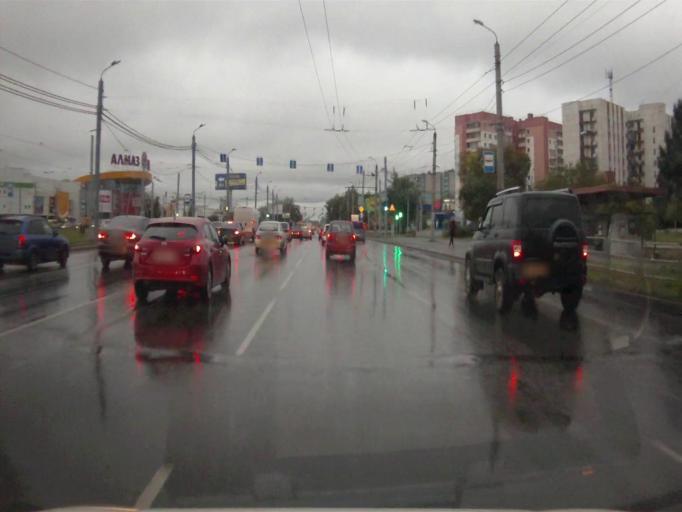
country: RU
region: Chelyabinsk
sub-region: Gorod Chelyabinsk
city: Chelyabinsk
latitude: 55.1465
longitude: 61.4458
